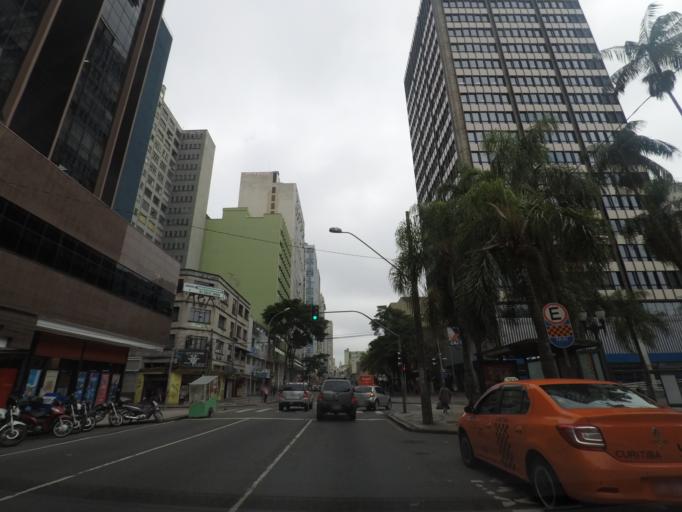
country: BR
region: Parana
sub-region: Curitiba
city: Curitiba
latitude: -25.4333
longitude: -49.2708
